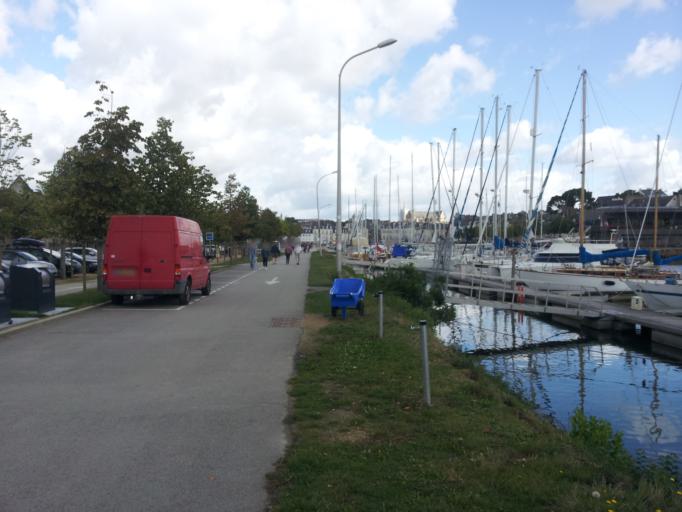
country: FR
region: Brittany
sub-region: Departement du Morbihan
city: Vannes
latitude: 47.6502
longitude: -2.7583
